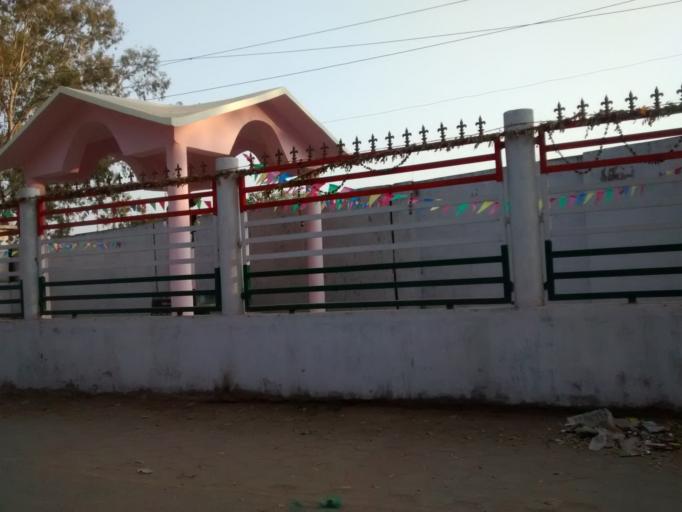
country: IN
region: Chhattisgarh
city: Gumla
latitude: 23.0385
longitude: 84.5385
